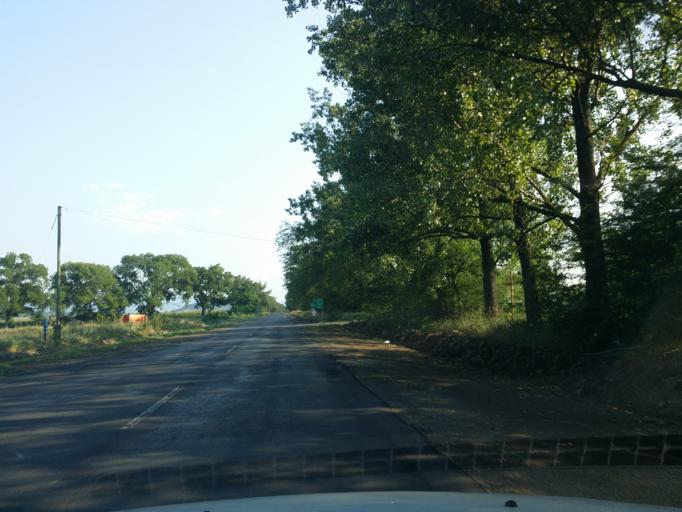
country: HU
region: Borsod-Abauj-Zemplen
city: Abaujszanto
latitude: 48.3629
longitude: 21.2156
